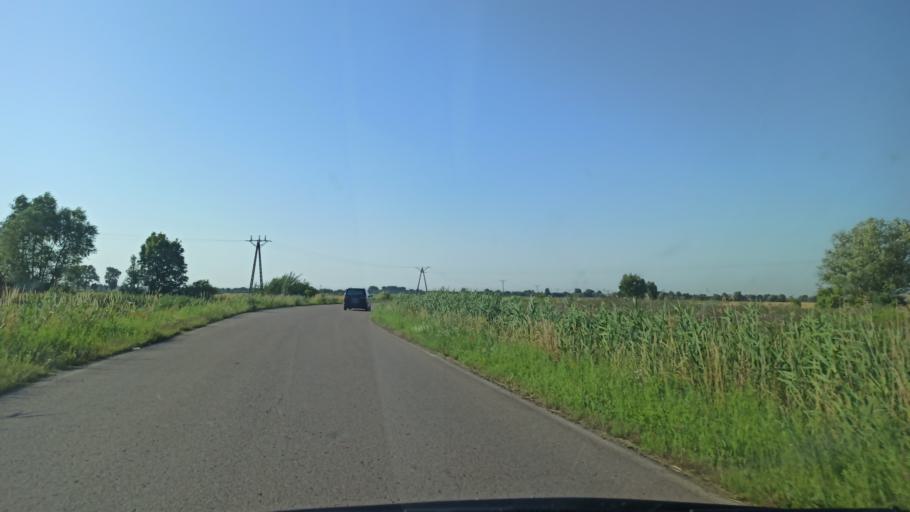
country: PL
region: Warmian-Masurian Voivodeship
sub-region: Powiat elblaski
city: Elblag
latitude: 54.1876
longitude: 19.3329
